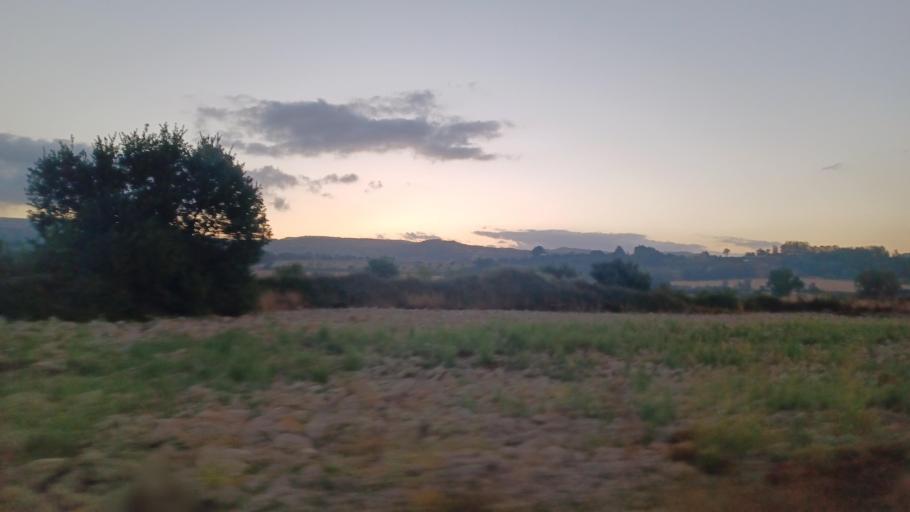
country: CY
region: Pafos
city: Mesogi
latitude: 34.8540
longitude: 32.5422
